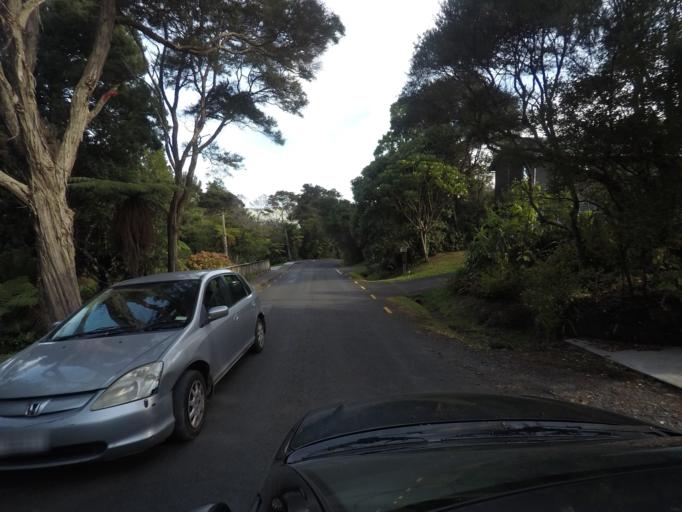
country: NZ
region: Auckland
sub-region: Auckland
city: Titirangi
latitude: -36.9986
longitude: 174.5720
